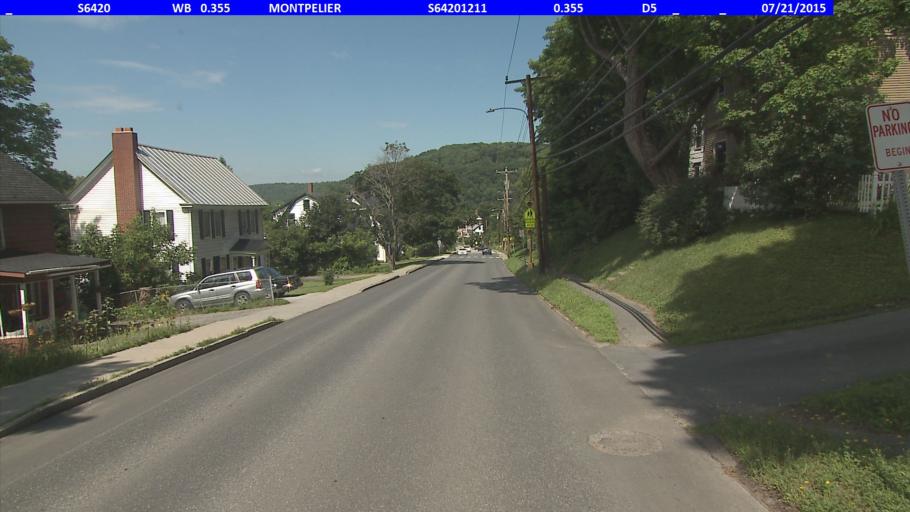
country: US
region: Vermont
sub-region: Washington County
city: Montpelier
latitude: 44.2619
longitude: -72.5656
